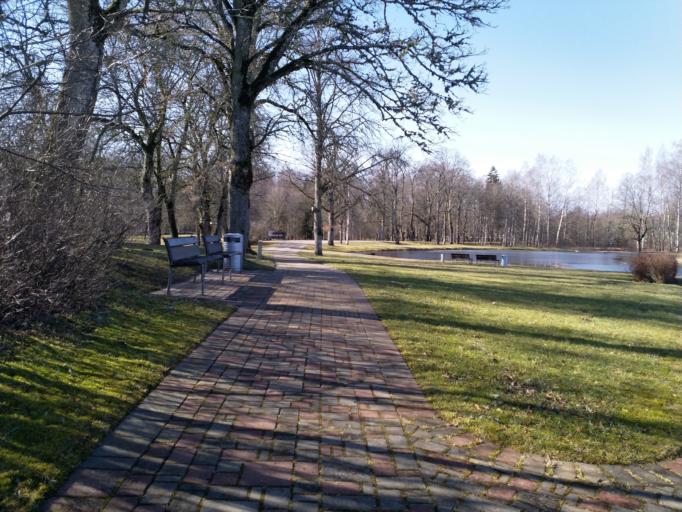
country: LV
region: Aizpute
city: Aizpute
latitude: 56.8333
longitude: 21.7759
